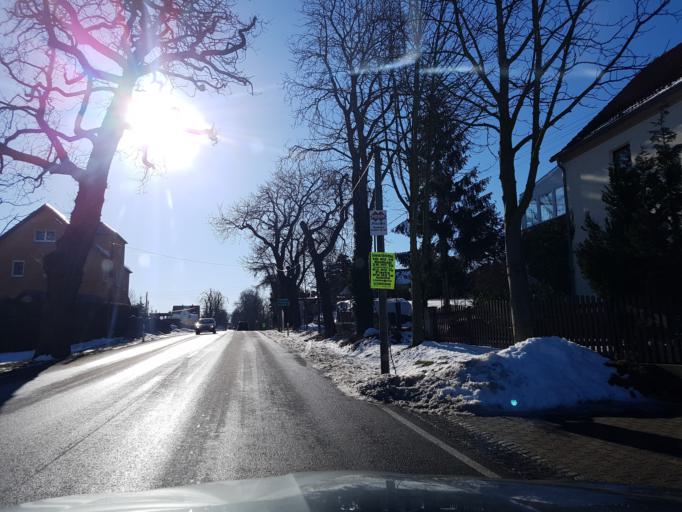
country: DE
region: Saxony
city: Moritzburg
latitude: 51.1315
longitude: 13.6852
